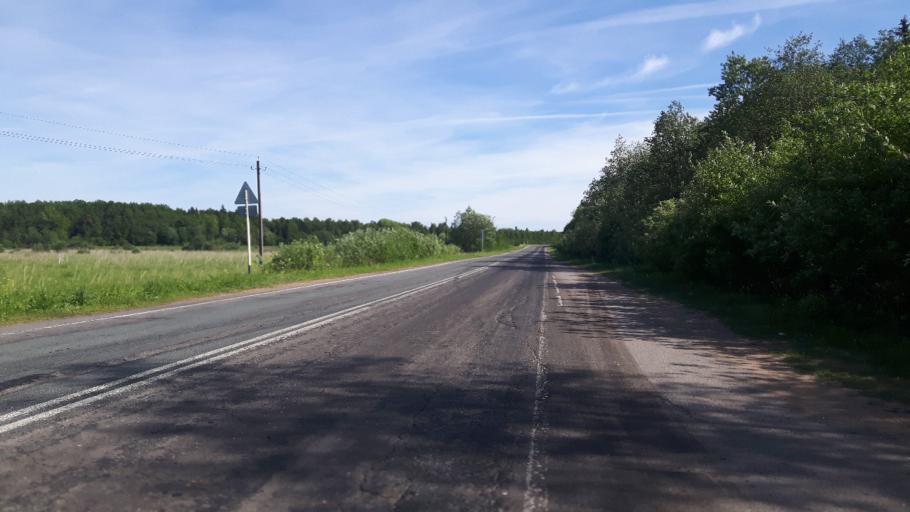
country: RU
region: Leningrad
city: Ivangorod
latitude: 59.4145
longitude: 28.3819
